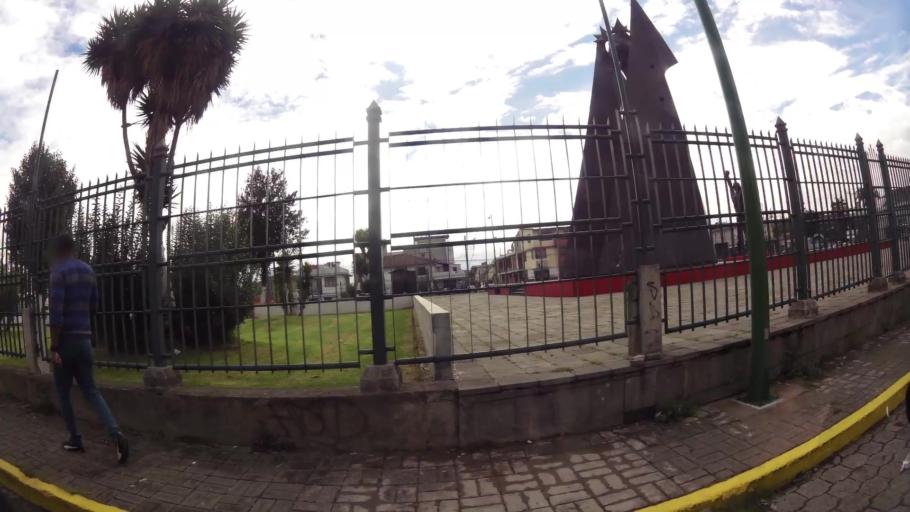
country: EC
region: Pichincha
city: Sangolqui
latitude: -0.3340
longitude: -78.4428
